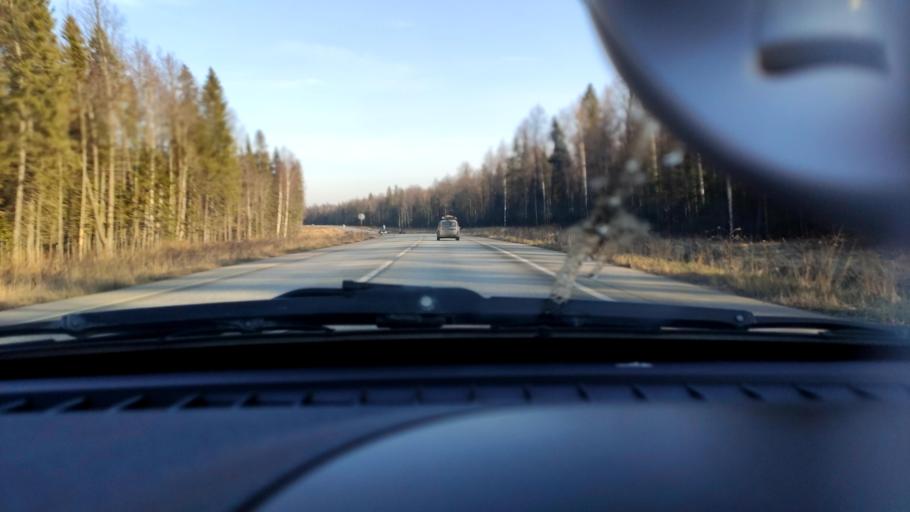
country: RU
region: Perm
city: Novyye Lyady
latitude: 58.0321
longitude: 56.5273
